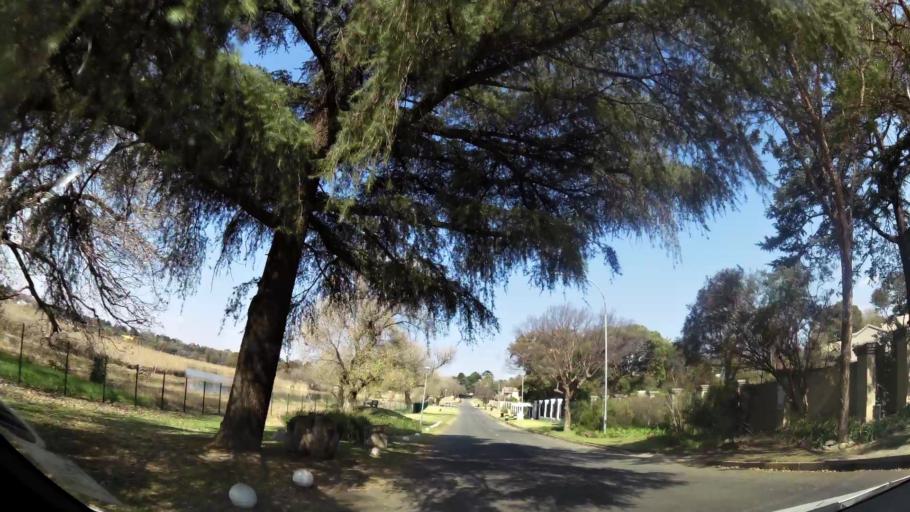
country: ZA
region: Gauteng
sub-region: Ekurhuleni Metropolitan Municipality
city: Benoni
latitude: -26.1934
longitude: 28.2904
